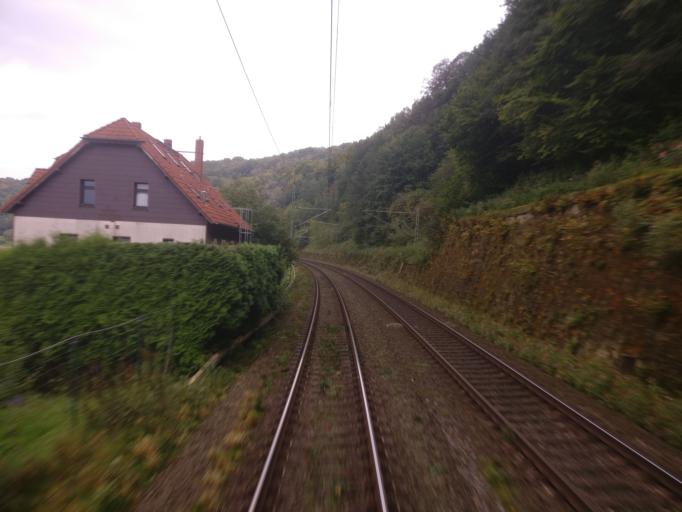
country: DE
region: Saxony
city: Struppen
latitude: 50.9440
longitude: 14.0047
